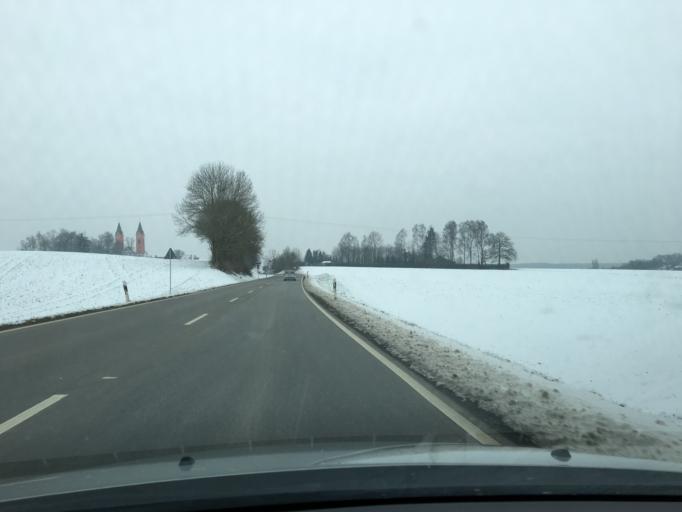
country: DE
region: Bavaria
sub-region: Lower Bavaria
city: Vilsbiburg
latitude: 48.4412
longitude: 12.3686
